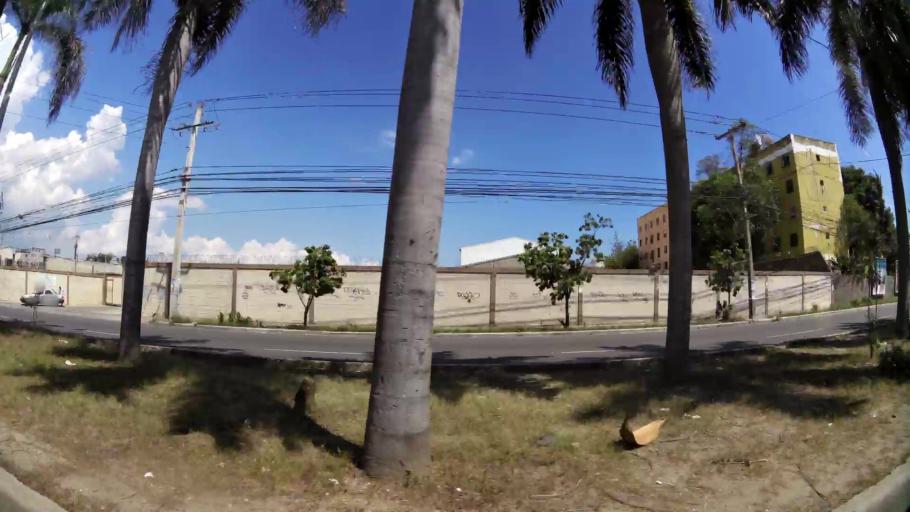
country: DO
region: Santo Domingo
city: Santo Domingo Oeste
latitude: 18.4664
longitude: -69.9949
